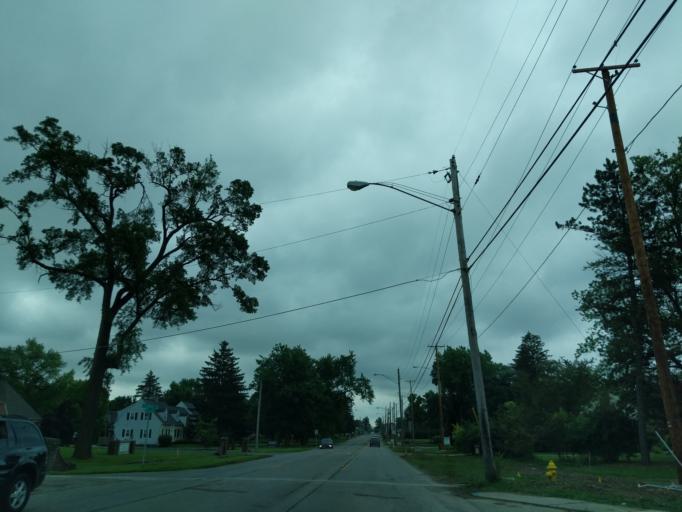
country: US
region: Indiana
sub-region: Delaware County
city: Muncie
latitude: 40.2137
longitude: -85.3996
